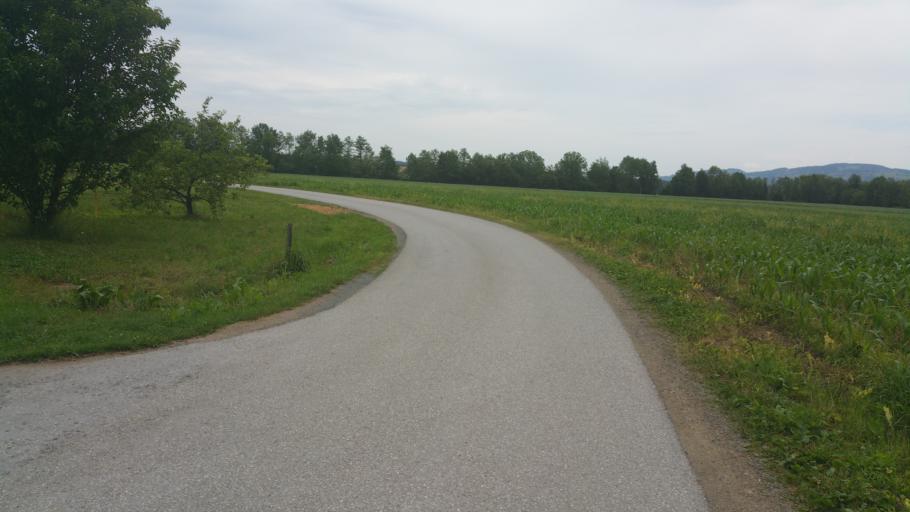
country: AT
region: Styria
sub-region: Politischer Bezirk Leibnitz
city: Gleinstatten
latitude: 46.7379
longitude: 15.3453
